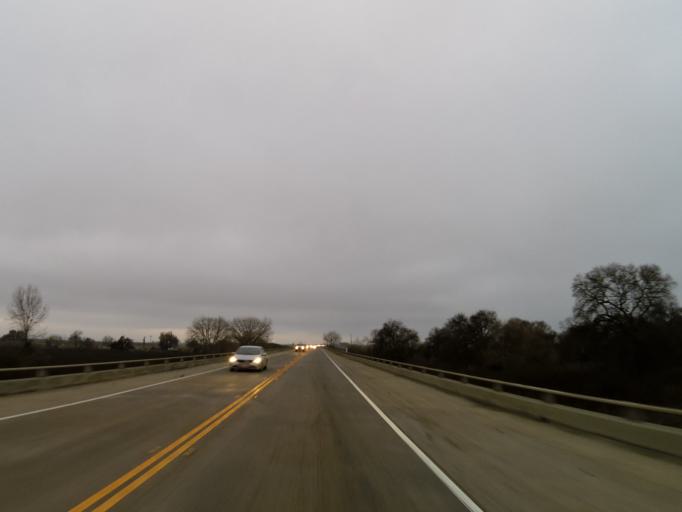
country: US
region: California
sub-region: San Joaquin County
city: Ripon
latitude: 37.6416
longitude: -121.2249
